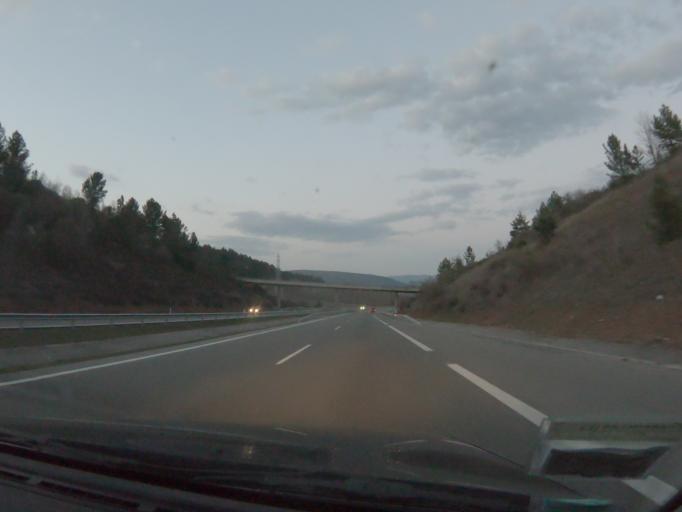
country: ES
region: Castille and Leon
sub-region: Provincia de Leon
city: Molinaseca
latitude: 42.5728
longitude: -6.5365
